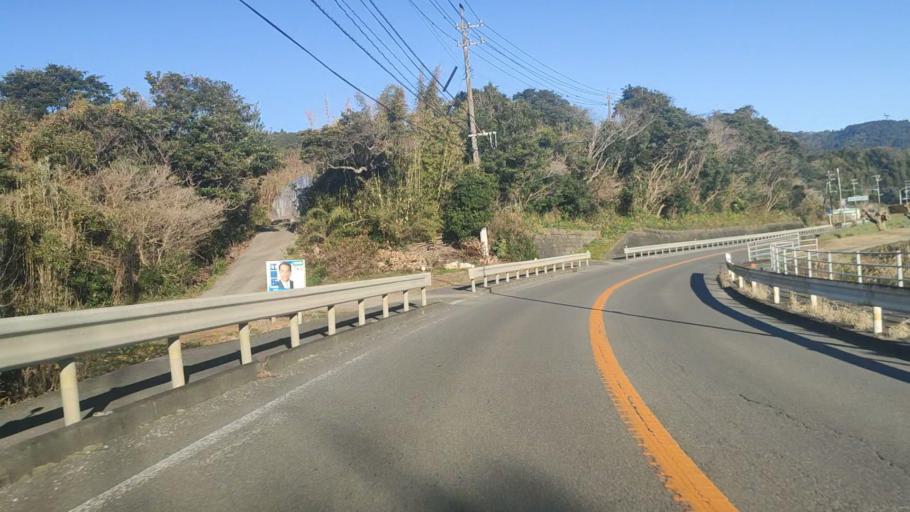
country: JP
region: Miyazaki
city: Nobeoka
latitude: 32.3540
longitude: 131.6213
